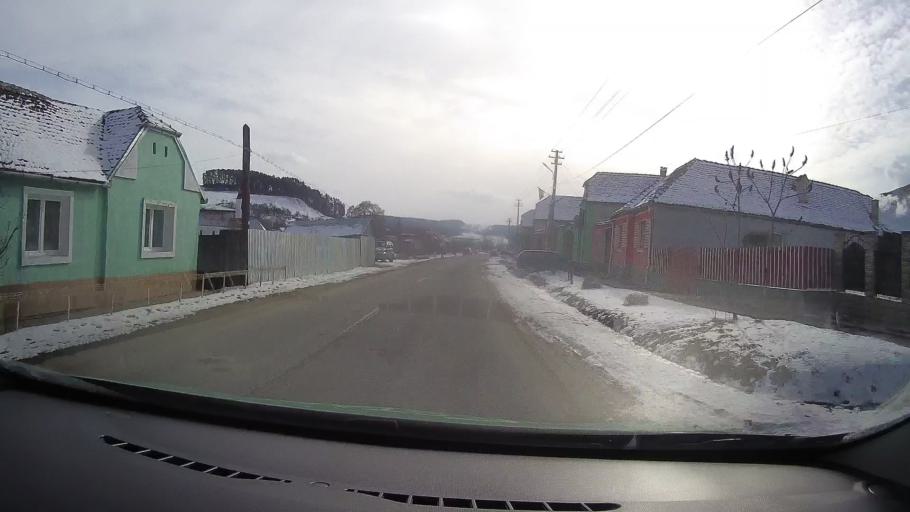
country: RO
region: Sibiu
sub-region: Comuna Bradeni
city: Bradeni
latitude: 46.0862
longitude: 24.8325
